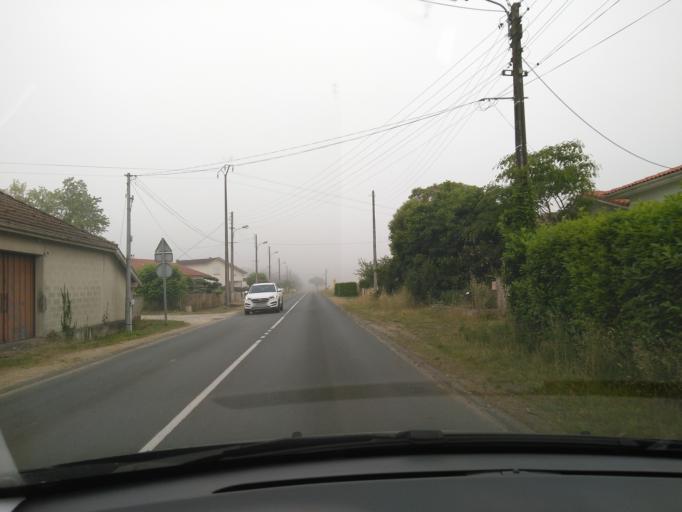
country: FR
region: Aquitaine
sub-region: Departement des Landes
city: Villeneuve-de-Marsan
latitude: 43.8910
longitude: -0.3145
